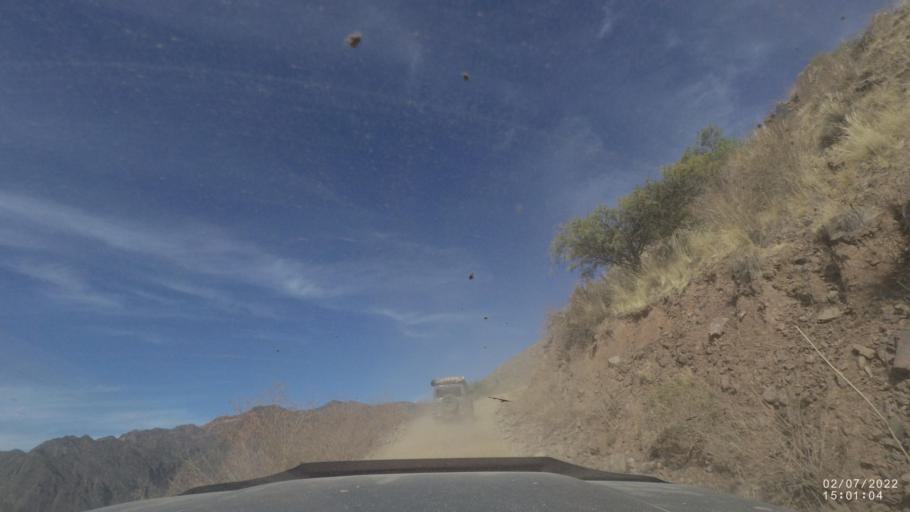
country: BO
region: Cochabamba
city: Irpa Irpa
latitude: -17.8528
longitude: -66.4418
